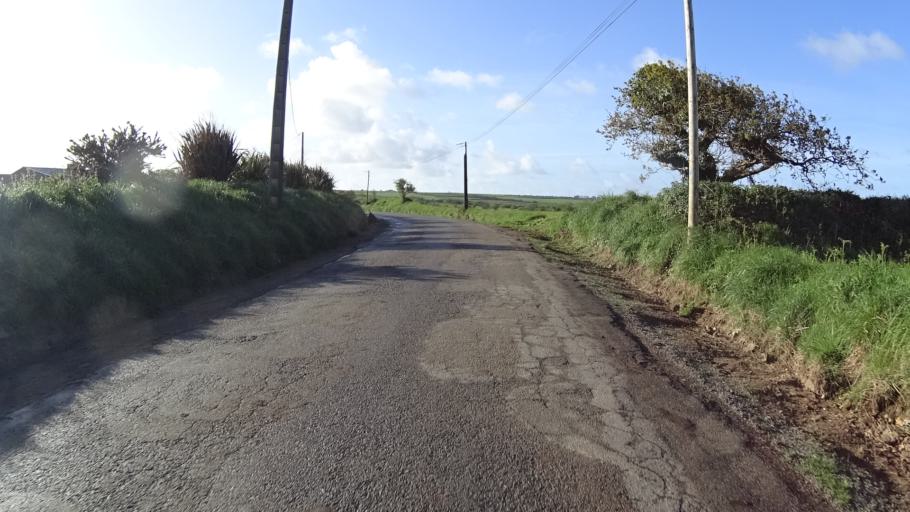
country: FR
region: Brittany
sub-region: Departement du Finistere
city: Plouarzel
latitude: 48.4304
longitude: -4.7144
